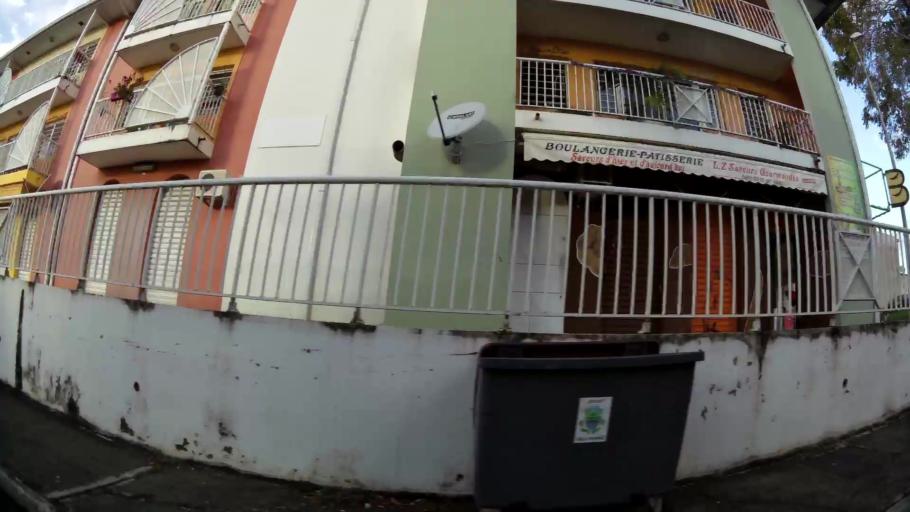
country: GP
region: Guadeloupe
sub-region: Guadeloupe
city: Petit-Bourg
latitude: 16.1330
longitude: -61.5722
